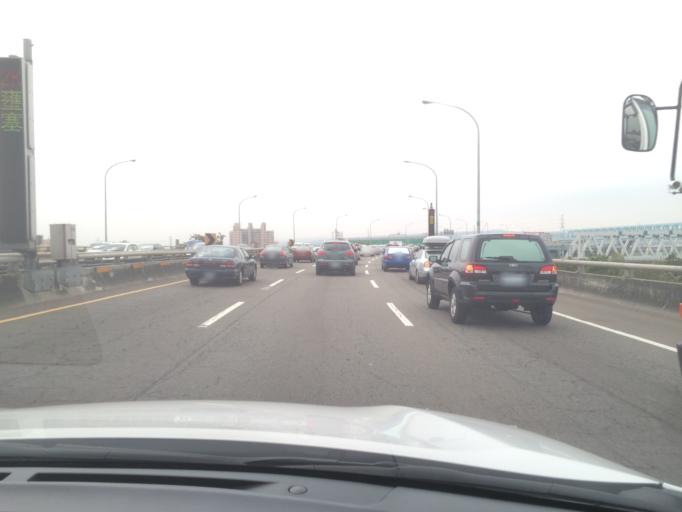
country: TW
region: Taiwan
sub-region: Changhua
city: Chang-hua
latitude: 24.1135
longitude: 120.6201
